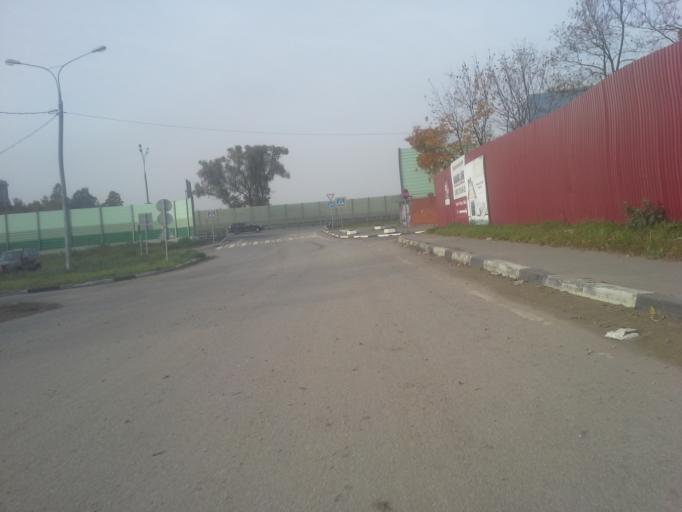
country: RU
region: Moskovskaya
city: Golitsyno
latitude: 55.6015
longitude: 36.9968
